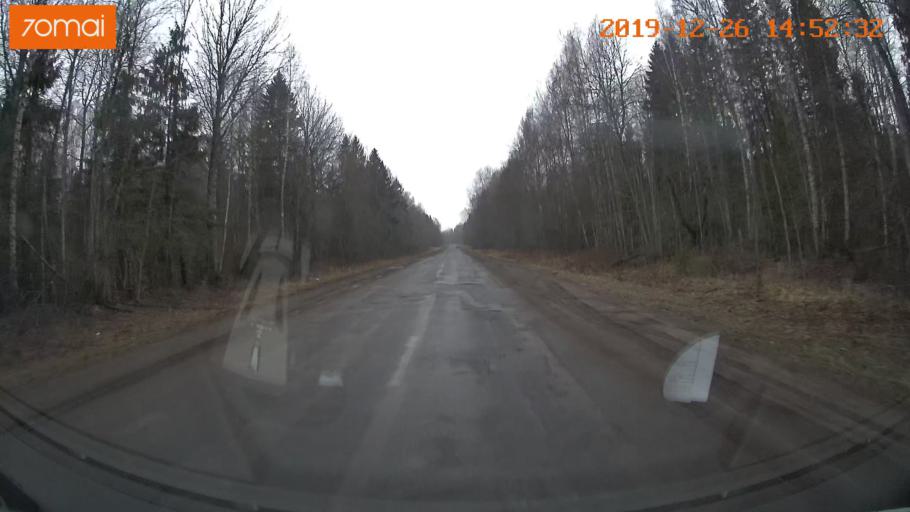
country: RU
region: Jaroslavl
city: Rybinsk
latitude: 58.3210
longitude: 38.8977
